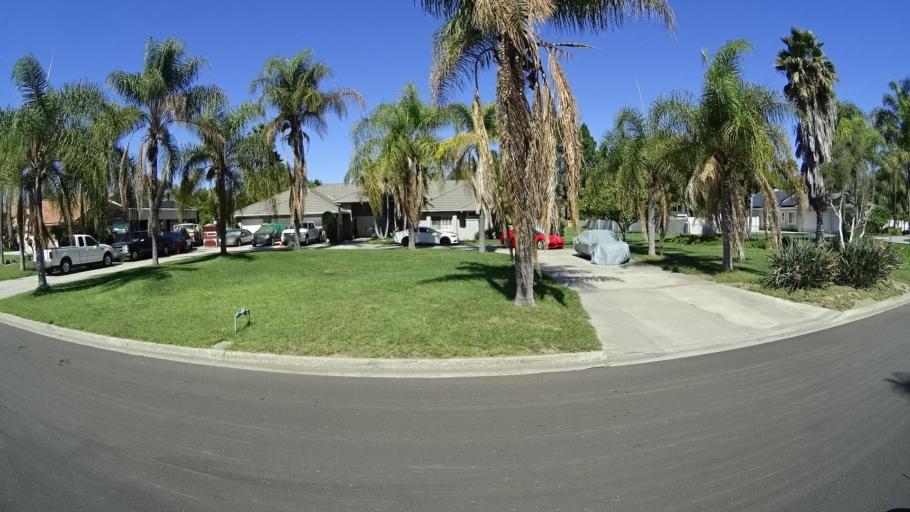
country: US
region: California
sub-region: San Diego County
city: Rancho San Diego
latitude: 32.7393
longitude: -116.9174
